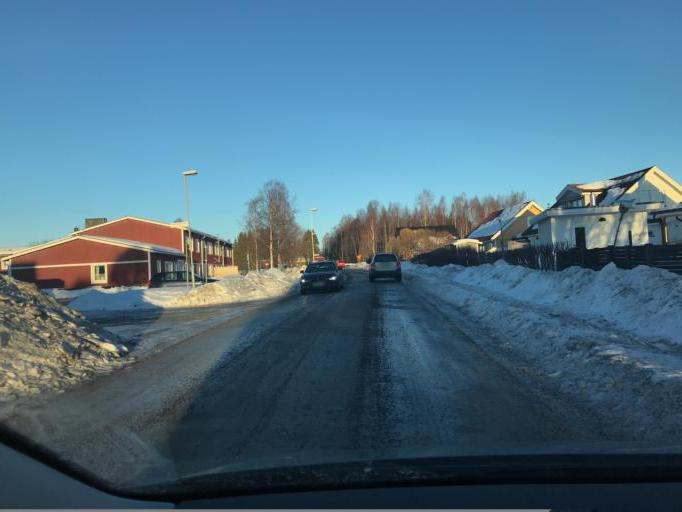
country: SE
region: Norrbotten
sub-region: Lulea Kommun
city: Sodra Sunderbyn
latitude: 65.6568
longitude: 21.9523
